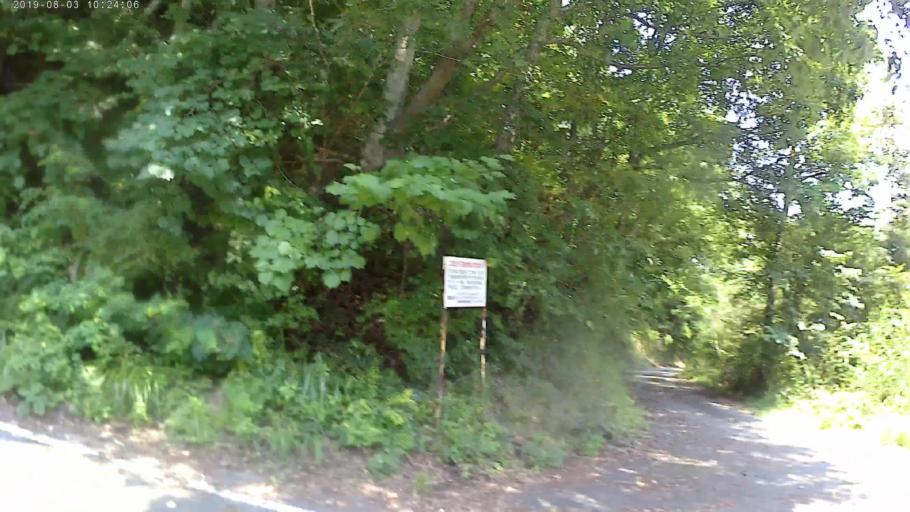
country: JP
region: Yamanashi
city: Enzan
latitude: 35.6300
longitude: 138.7691
